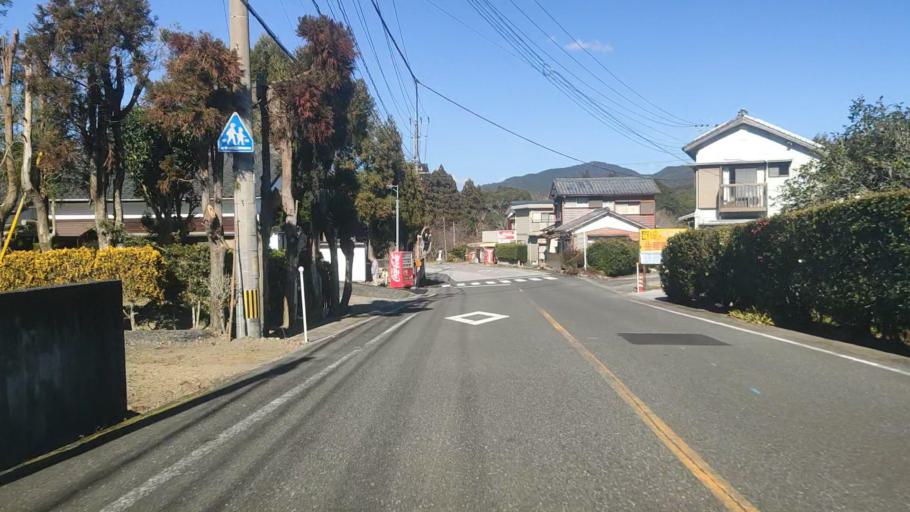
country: JP
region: Oita
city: Saiki
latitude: 32.9030
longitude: 131.9332
